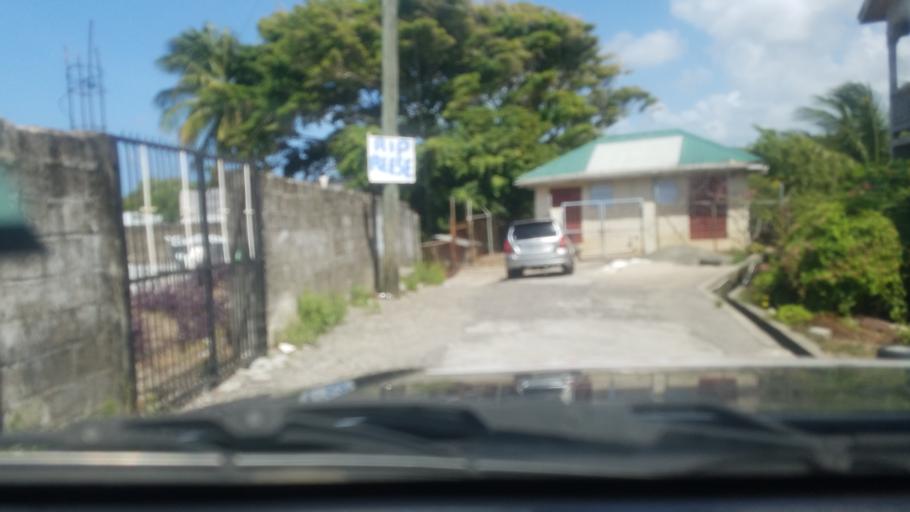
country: LC
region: Vieux-Fort
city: Vieux Fort
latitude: 13.7289
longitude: -60.9568
